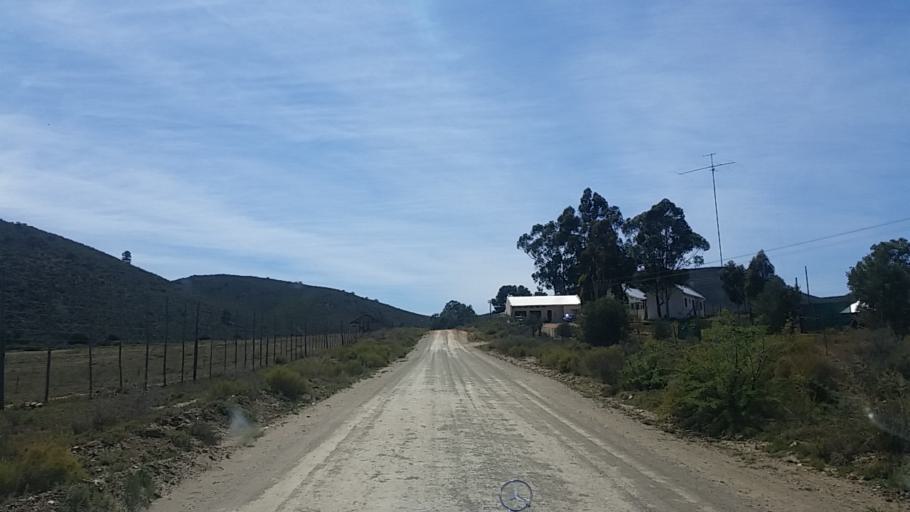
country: ZA
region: Western Cape
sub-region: Eden District Municipality
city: Knysna
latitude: -33.6428
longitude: 23.1395
